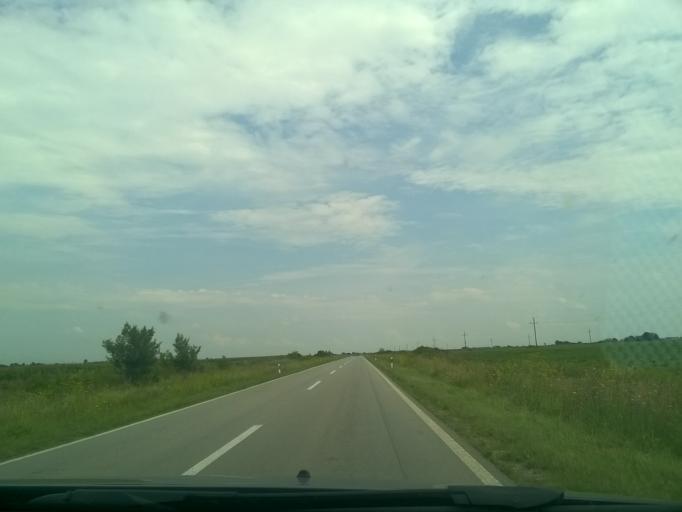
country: RS
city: Velika Greda
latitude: 45.2519
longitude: 21.0699
